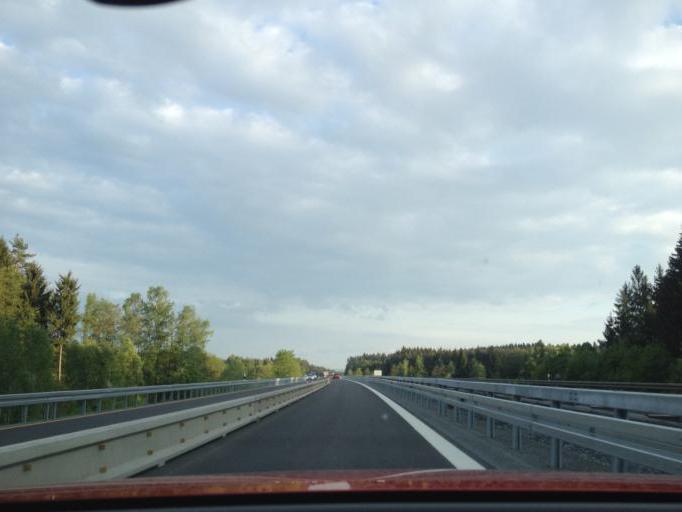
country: DE
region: Bavaria
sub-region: Upper Palatinate
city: Windischeschenbach
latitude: 49.7648
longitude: 12.1520
